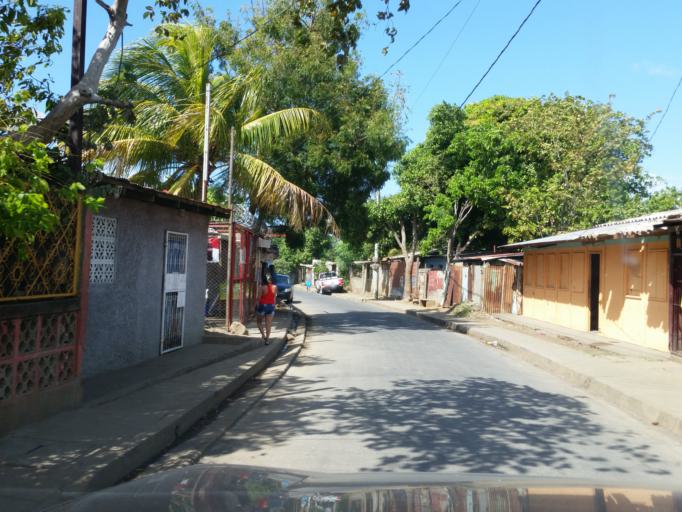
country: NI
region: Managua
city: Managua
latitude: 12.1168
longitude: -86.2404
